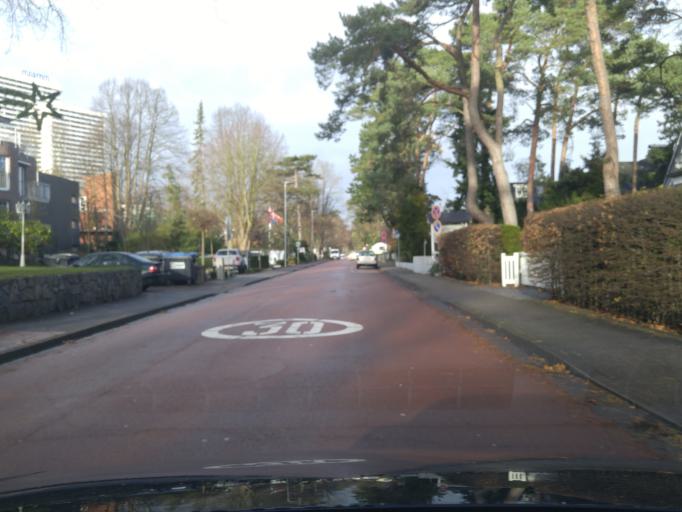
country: DE
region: Schleswig-Holstein
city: Timmendorfer Strand
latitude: 54.0035
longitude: 10.7764
